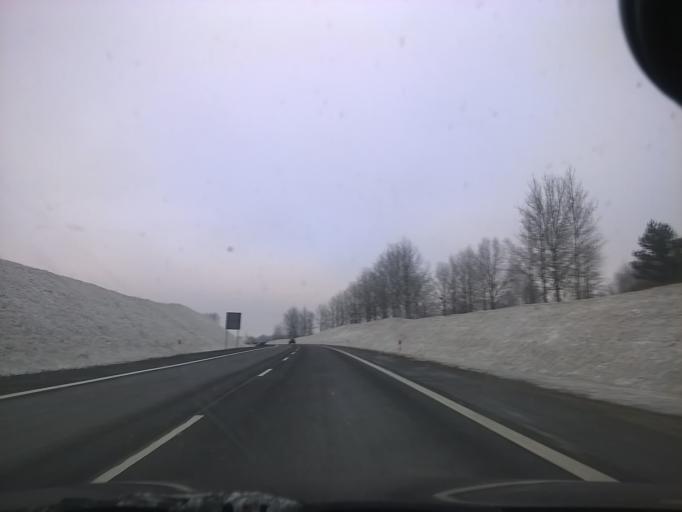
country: PL
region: Warmian-Masurian Voivodeship
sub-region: Powiat olsztynski
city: Czerwonka
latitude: 53.8262
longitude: 20.8522
